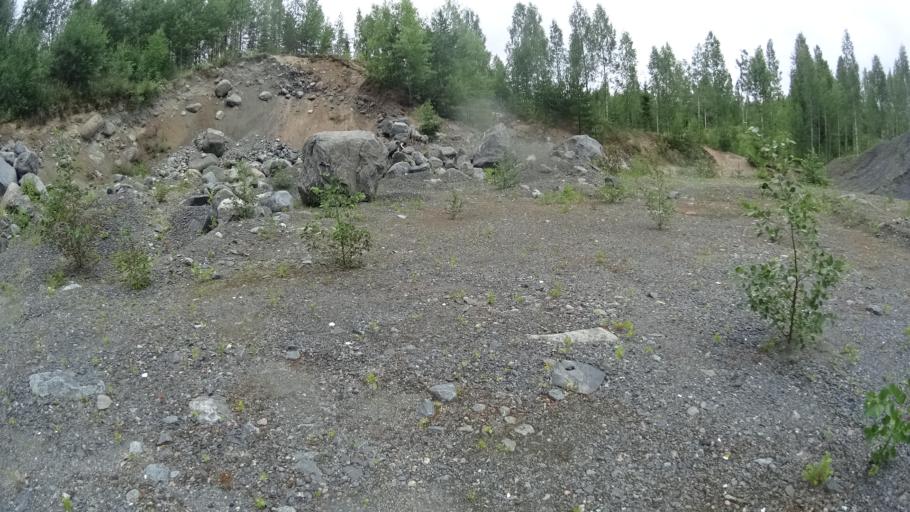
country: FI
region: Uusimaa
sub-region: Helsinki
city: Karkkila
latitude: 60.5797
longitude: 24.2762
